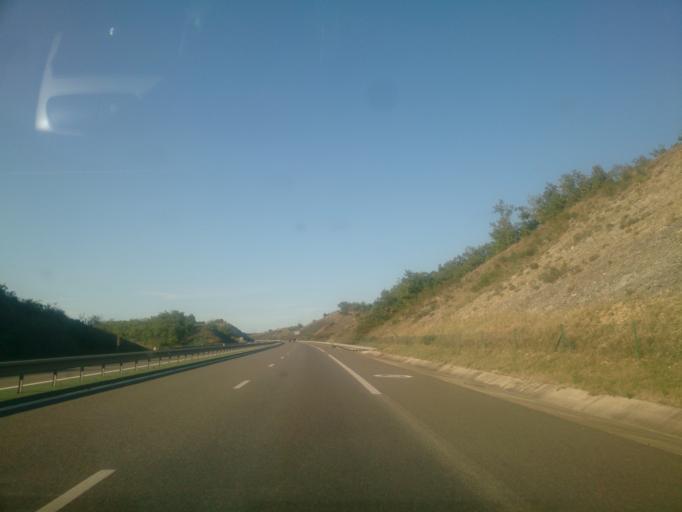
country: FR
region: Midi-Pyrenees
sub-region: Departement du Lot
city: Cahors
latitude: 44.5143
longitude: 1.5051
